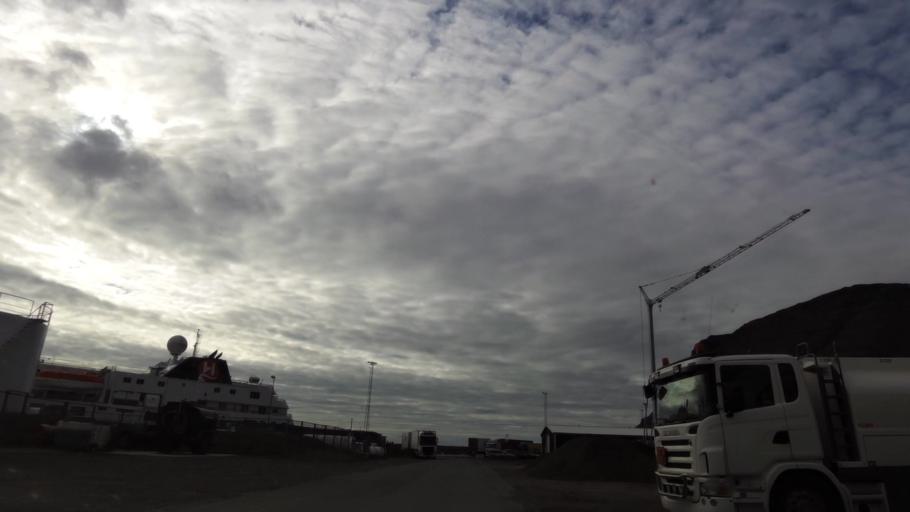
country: IS
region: West
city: Olafsvik
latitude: 65.5955
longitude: -24.0033
